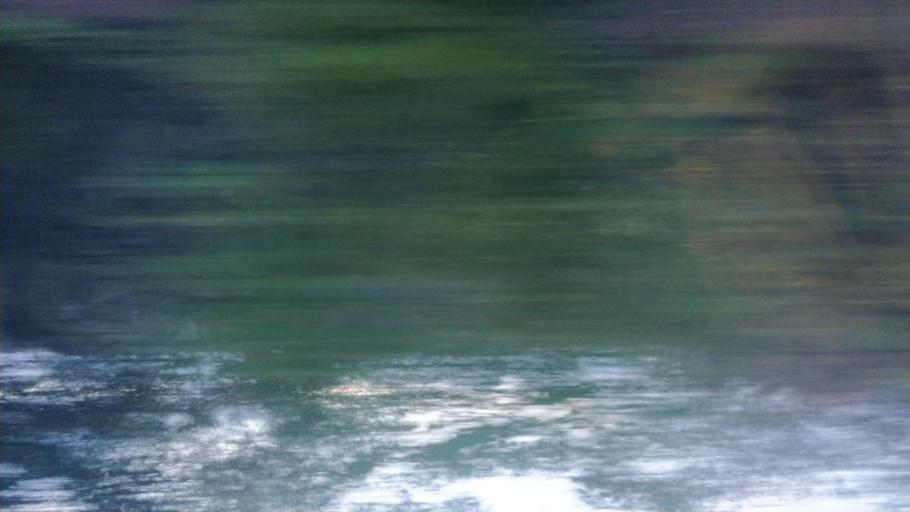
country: GB
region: England
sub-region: Borough of Wigan
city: Shevington
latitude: 53.5661
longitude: -2.7078
